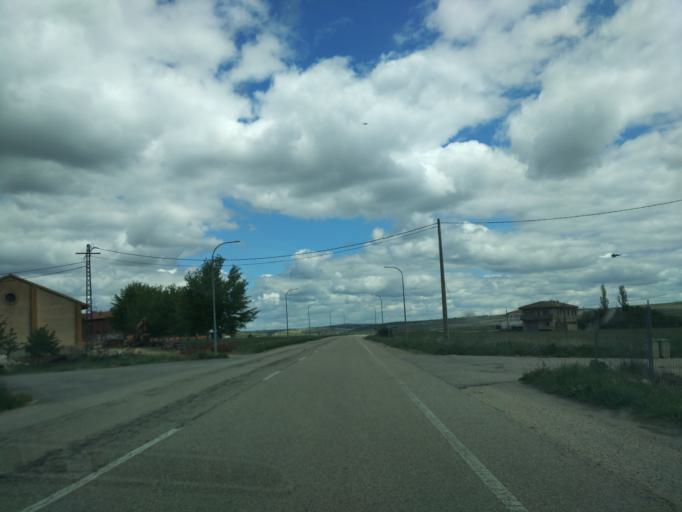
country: ES
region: Castille-La Mancha
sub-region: Provincia de Guadalajara
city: Torremocha del Campo
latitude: 40.9794
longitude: -2.6171
